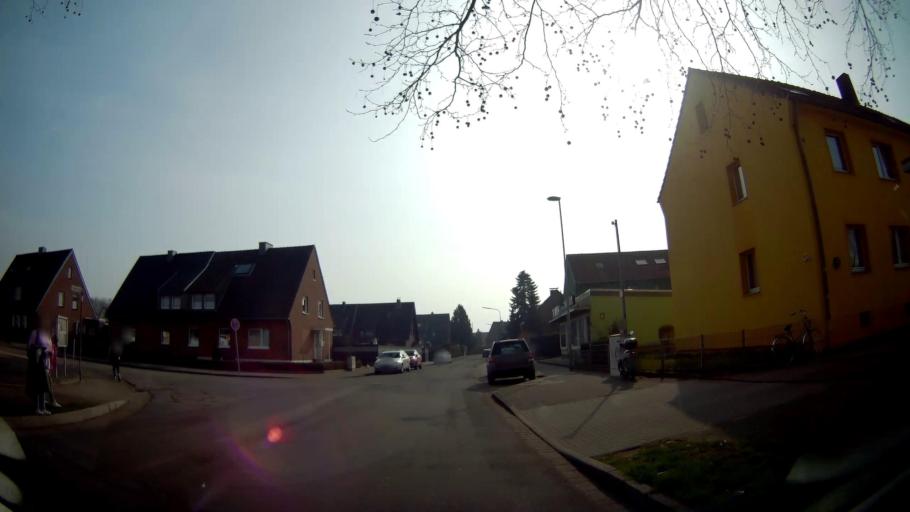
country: DE
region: North Rhine-Westphalia
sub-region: Regierungsbezirk Dusseldorf
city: Moers
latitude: 51.4853
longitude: 6.6380
